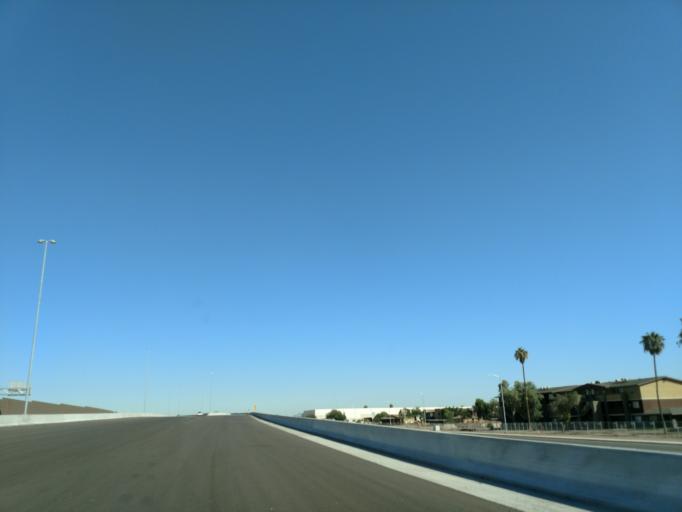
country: US
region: Arizona
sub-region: Maricopa County
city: Tolleson
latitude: 33.4558
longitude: -112.1853
